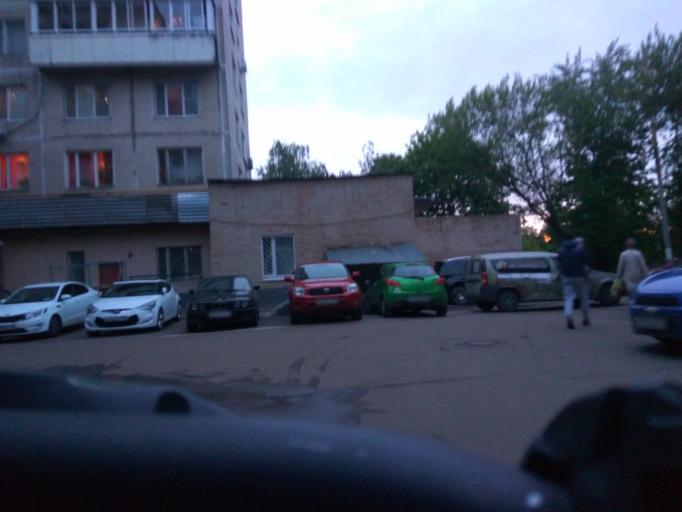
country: RU
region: Moscow
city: Kolomenskoye
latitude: 55.6705
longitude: 37.6506
